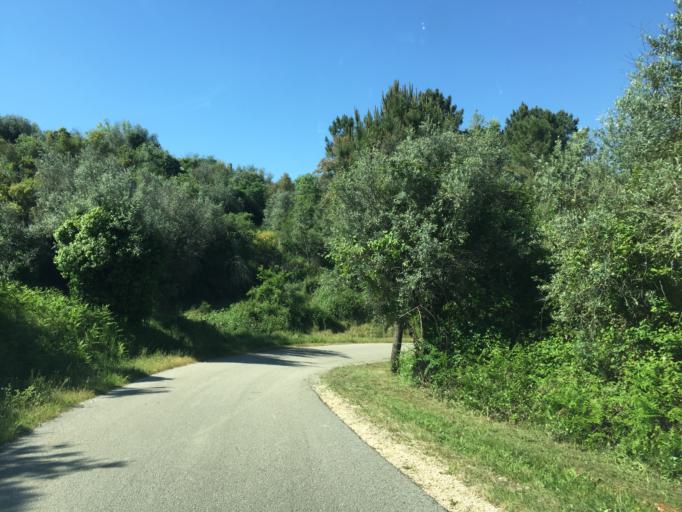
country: PT
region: Leiria
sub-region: Alvaiazere
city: Alvaiazere
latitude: 39.8412
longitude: -8.3788
